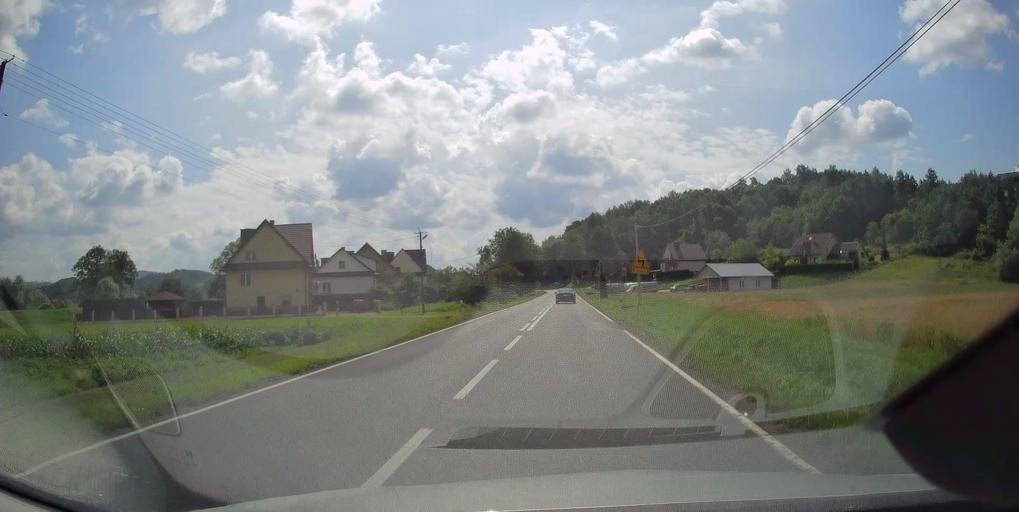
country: PL
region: Lesser Poland Voivodeship
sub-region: Powiat tarnowski
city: Janowice
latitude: 49.8883
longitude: 20.8262
